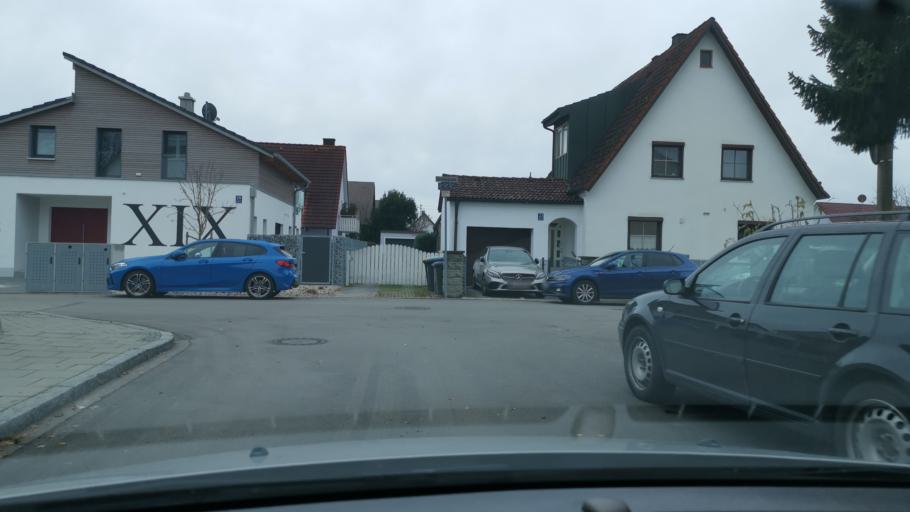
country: DE
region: Bavaria
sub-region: Upper Bavaria
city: Unterschleissheim
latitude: 48.2838
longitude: 11.5838
